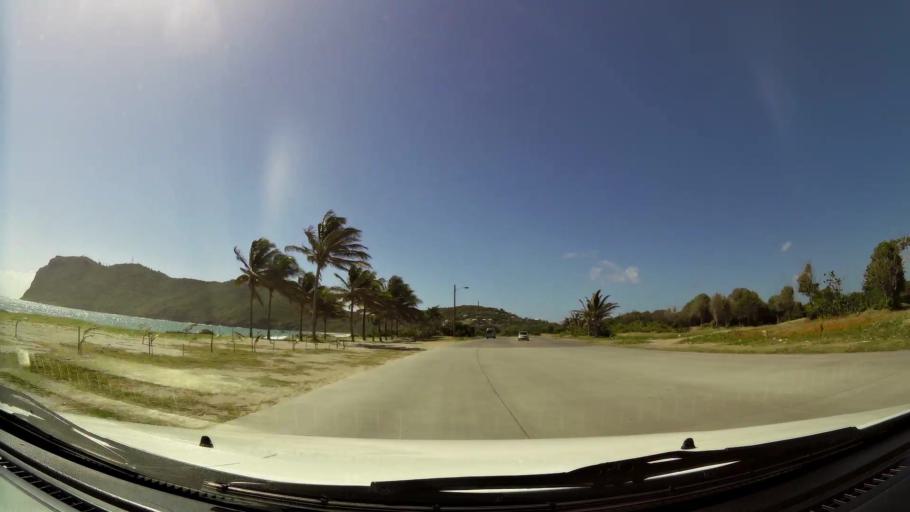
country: LC
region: Vieux-Fort
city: Vieux Fort
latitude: 13.7294
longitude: -60.9438
